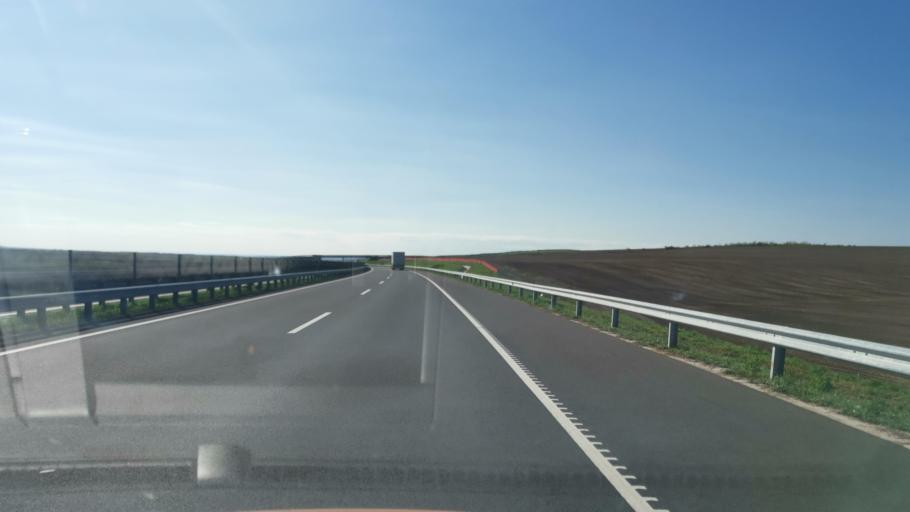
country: HU
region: Borsod-Abauj-Zemplen
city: Halmaj
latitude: 48.2834
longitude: 21.0118
